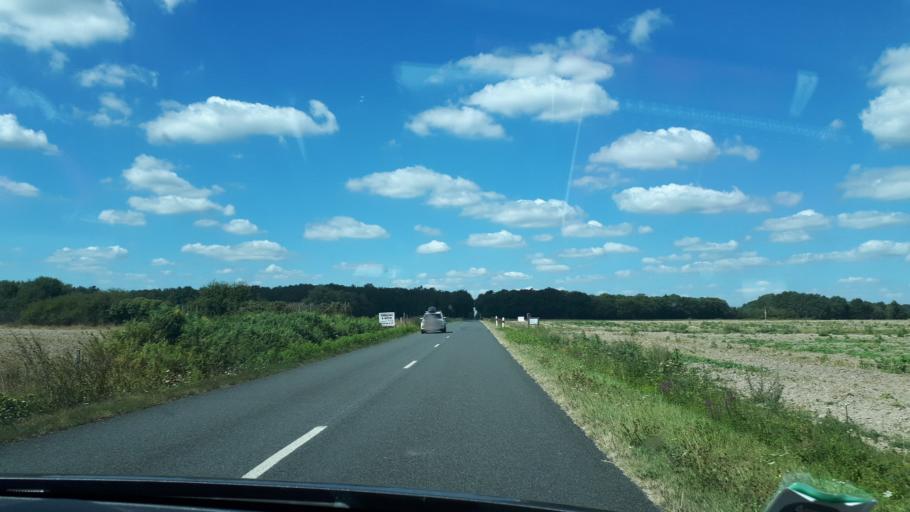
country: FR
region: Centre
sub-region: Departement du Loir-et-Cher
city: Neung-sur-Beuvron
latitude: 47.5341
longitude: 1.7330
